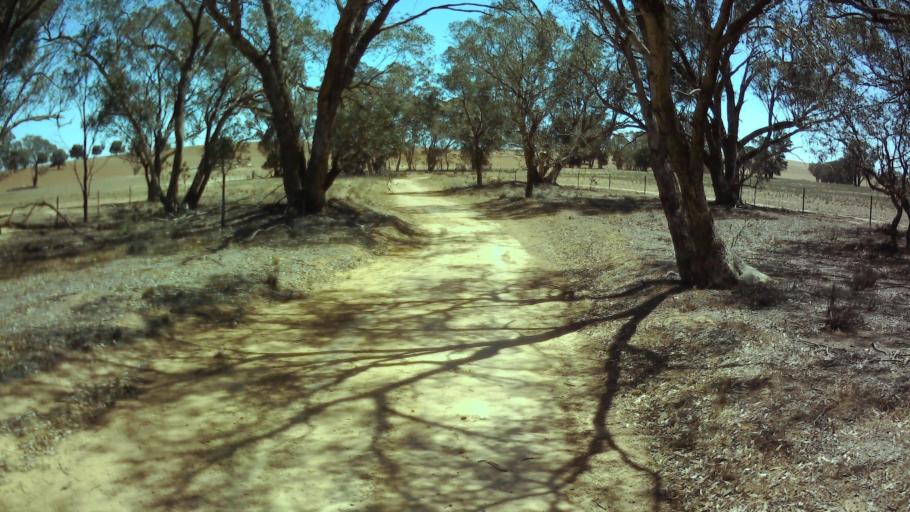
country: AU
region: New South Wales
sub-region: Weddin
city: Grenfell
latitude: -33.9871
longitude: 148.1642
